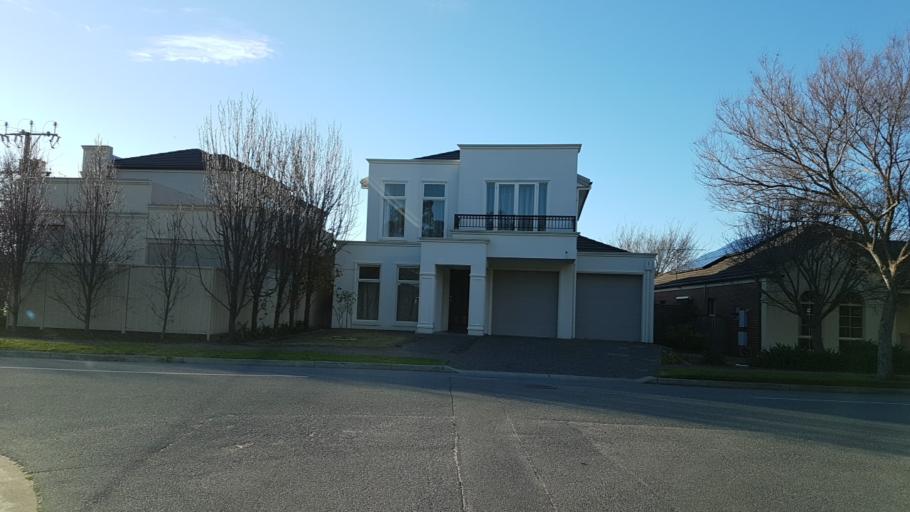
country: AU
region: South Australia
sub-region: Charles Sturt
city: Henley Beach
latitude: -34.9327
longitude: 138.5062
